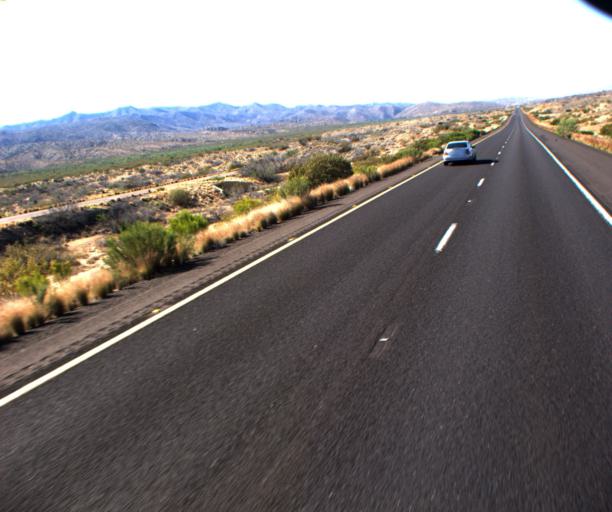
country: US
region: Arizona
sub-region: Mohave County
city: Kingman
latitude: 35.0654
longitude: -113.6657
